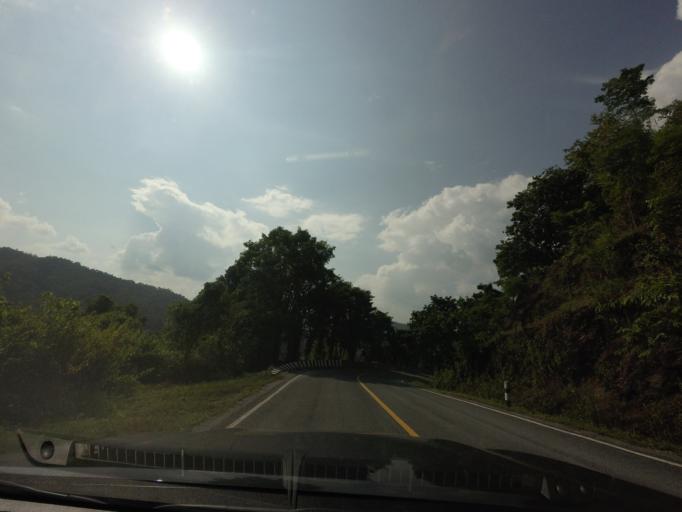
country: TH
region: Uttaradit
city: Ban Khok
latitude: 18.2530
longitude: 100.9951
